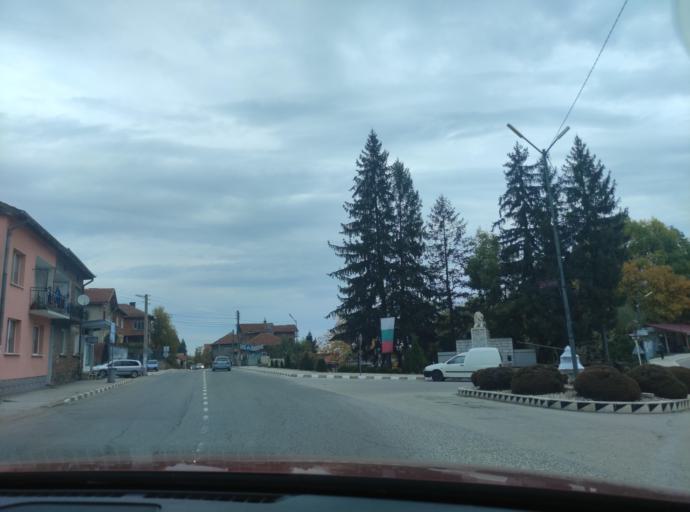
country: BG
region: Montana
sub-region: Obshtina Berkovitsa
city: Berkovitsa
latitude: 43.2004
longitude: 23.1617
